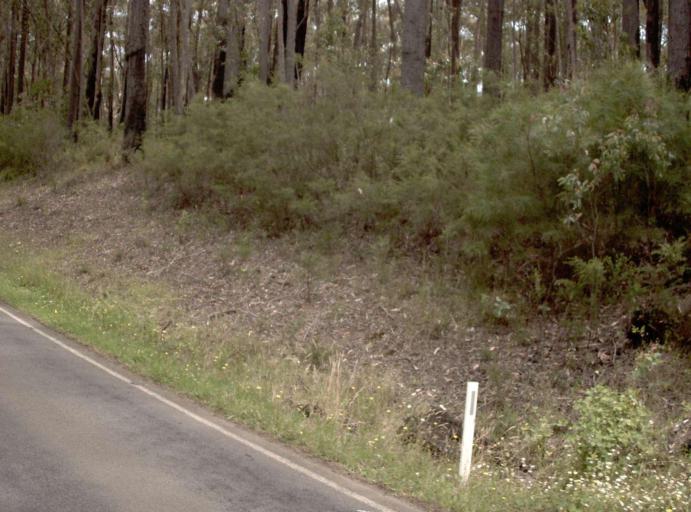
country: AU
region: Victoria
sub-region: Latrobe
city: Traralgon
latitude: -38.0147
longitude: 146.4203
